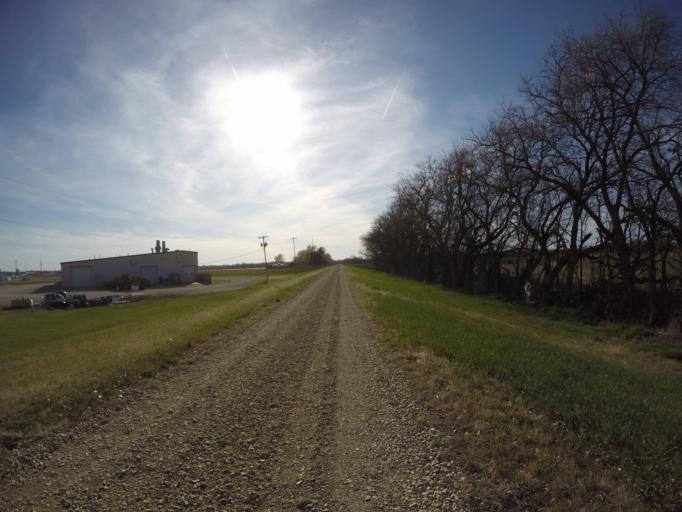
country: US
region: Kansas
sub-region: Saline County
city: Salina
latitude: 38.8633
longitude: -97.5923
